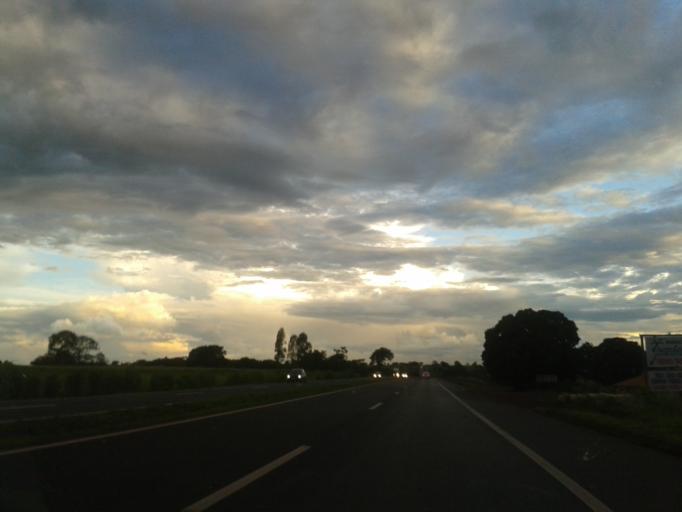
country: BR
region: Minas Gerais
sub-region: Centralina
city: Centralina
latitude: -18.6510
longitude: -49.1725
